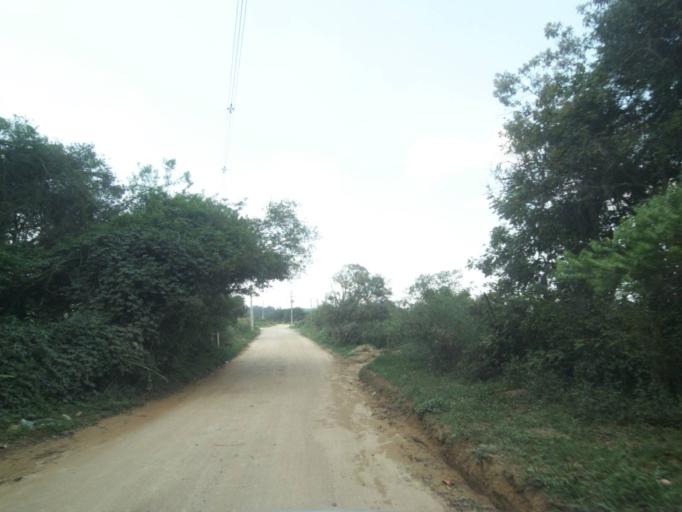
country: BR
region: Parana
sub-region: Sao Jose Dos Pinhais
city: Sao Jose dos Pinhais
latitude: -25.5420
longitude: -49.2335
